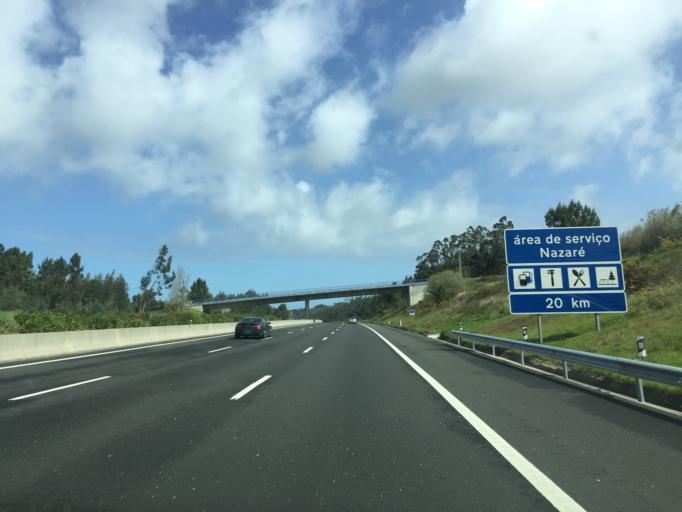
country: PT
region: Leiria
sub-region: Caldas da Rainha
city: Caldas da Rainha
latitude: 39.4701
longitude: -9.1088
